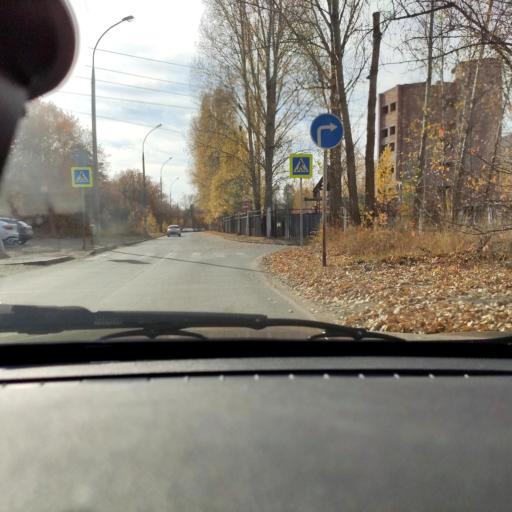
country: RU
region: Samara
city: Tol'yatti
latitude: 53.5036
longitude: 49.3043
